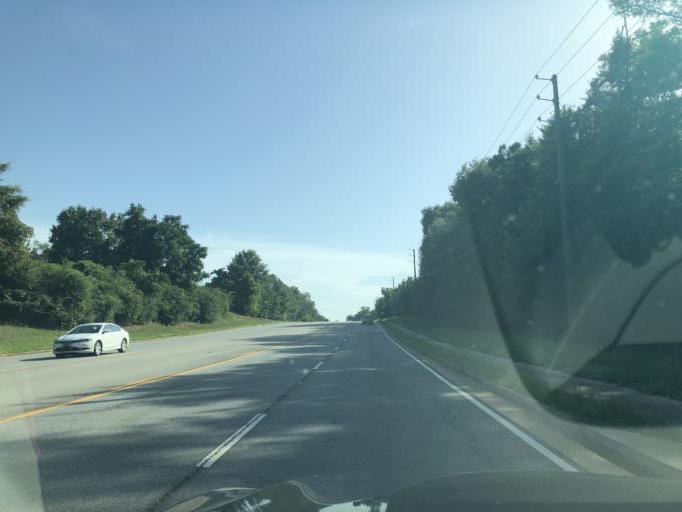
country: US
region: Georgia
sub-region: Muscogee County
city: Columbus
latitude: 32.5071
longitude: -84.8953
